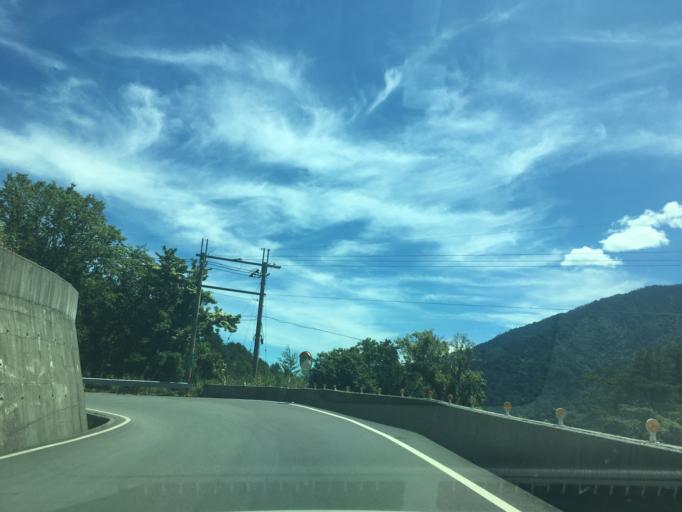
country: TW
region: Taiwan
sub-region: Nantou
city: Puli
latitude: 24.2371
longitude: 121.2535
